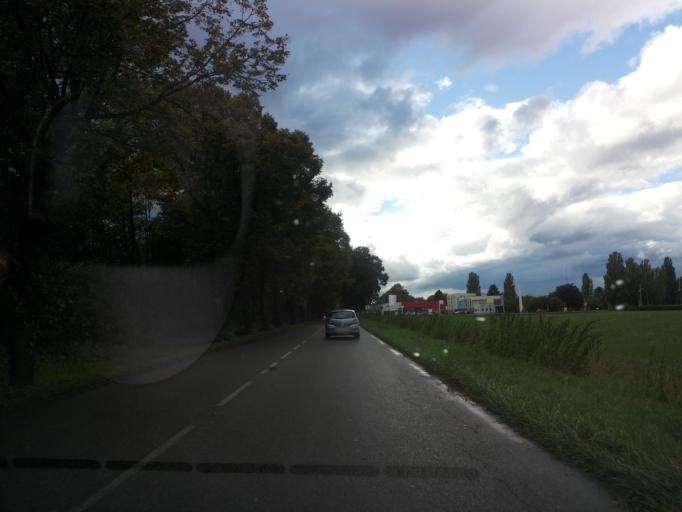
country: FR
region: Alsace
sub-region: Departement du Haut-Rhin
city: Riedisheim
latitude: 47.7562
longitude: 7.3829
